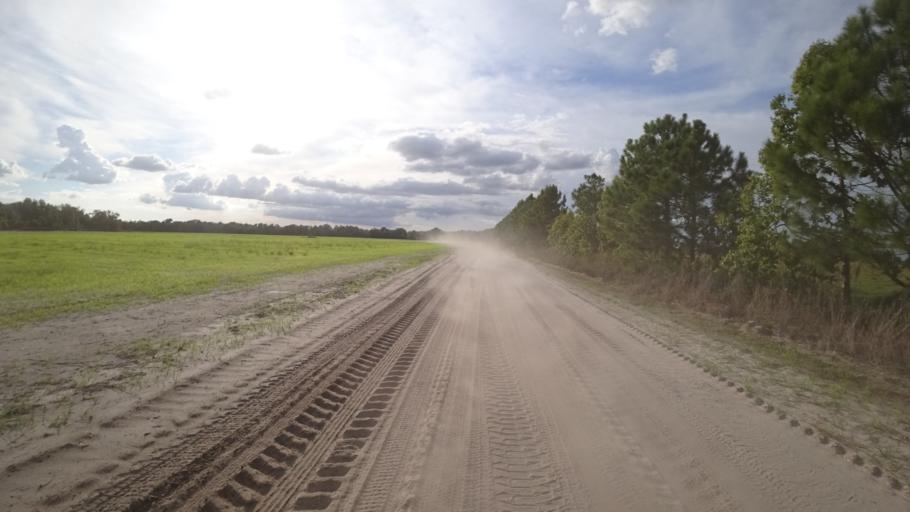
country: US
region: Florida
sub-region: Hillsborough County
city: Wimauma
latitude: 27.5664
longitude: -82.0860
